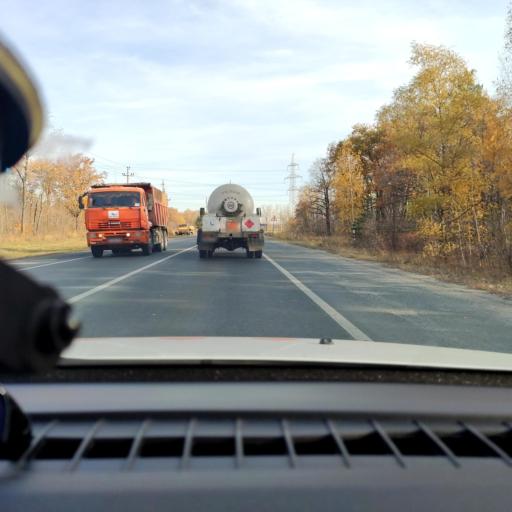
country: RU
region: Samara
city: Volzhskiy
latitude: 53.4485
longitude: 50.1234
